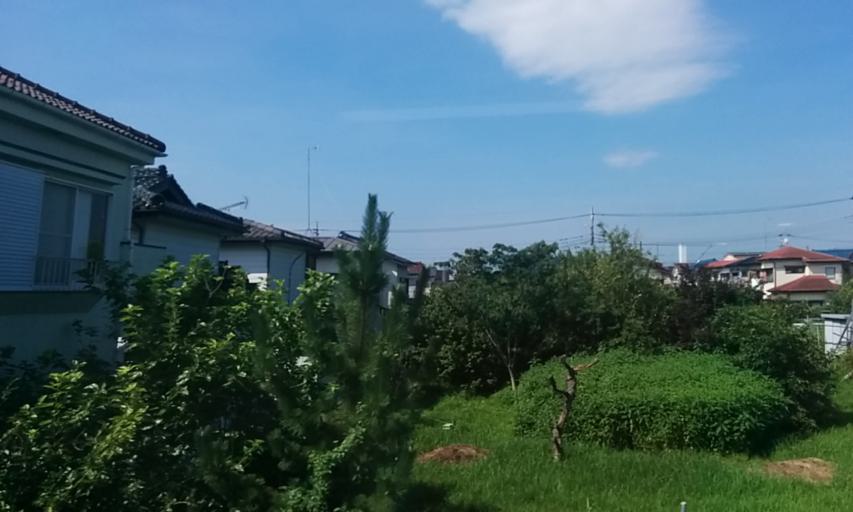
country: JP
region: Saitama
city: Kazo
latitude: 36.1268
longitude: 139.5897
